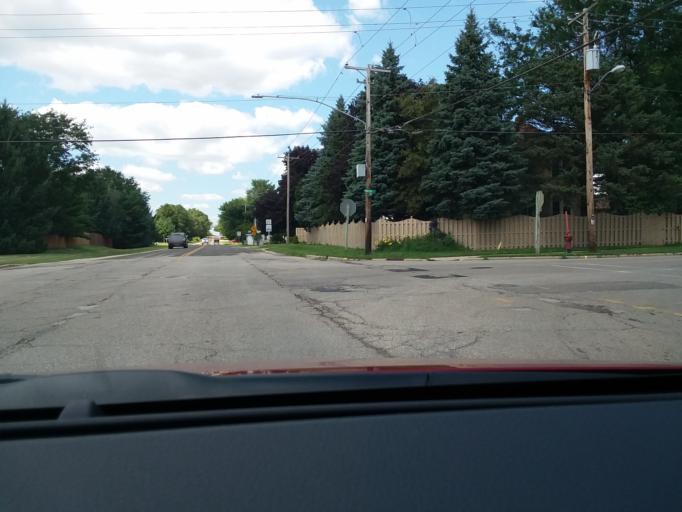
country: US
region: Wisconsin
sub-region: Dane County
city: Windsor
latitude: 43.2163
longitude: -89.3433
